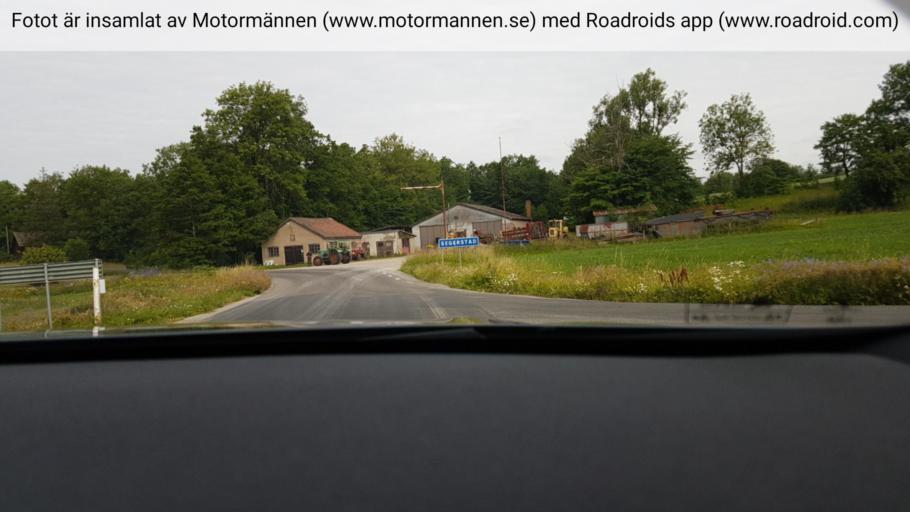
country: SE
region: Vaestra Goetaland
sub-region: Falkopings Kommun
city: Akarp
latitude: 58.2571
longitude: 13.6704
